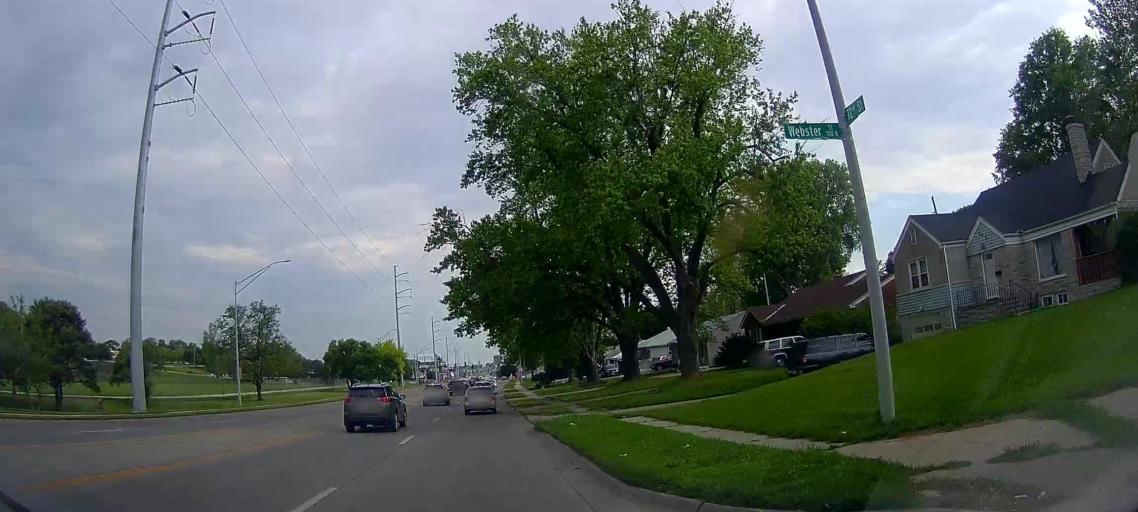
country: US
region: Nebraska
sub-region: Douglas County
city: Ralston
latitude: 41.2654
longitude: -96.0237
